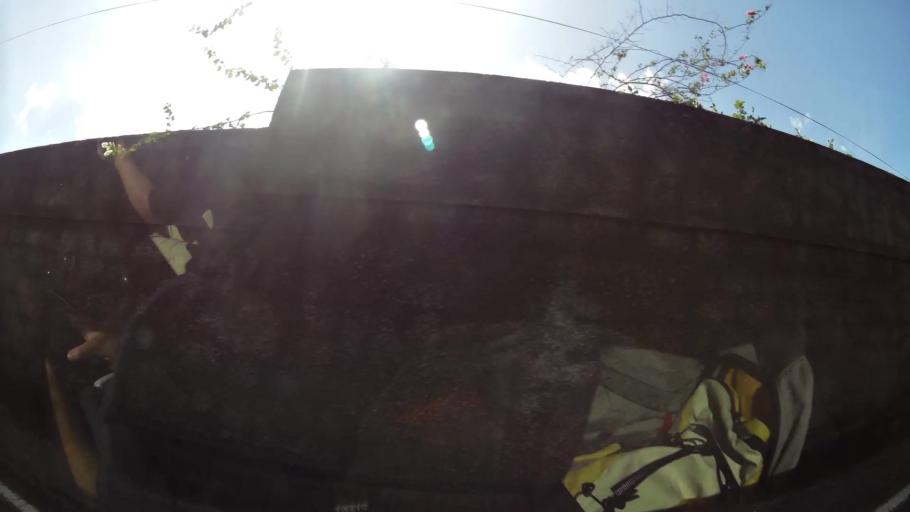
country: MQ
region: Martinique
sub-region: Martinique
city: Fort-de-France
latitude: 14.6205
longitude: -61.1056
